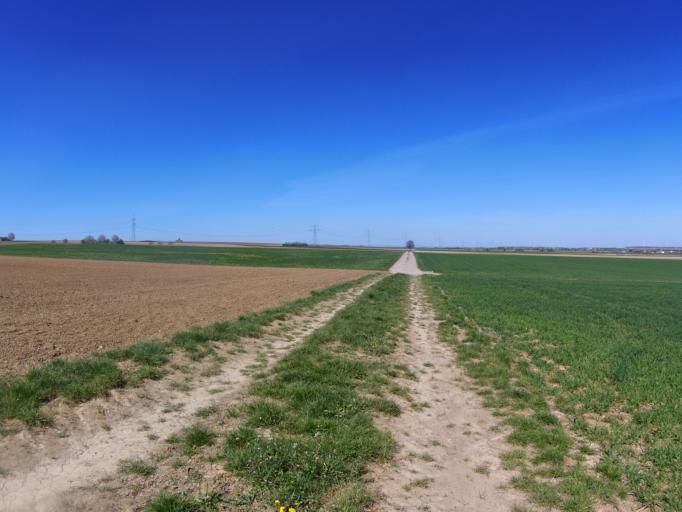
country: DE
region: Bavaria
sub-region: Regierungsbezirk Unterfranken
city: Biebelried
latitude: 49.8046
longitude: 10.0887
